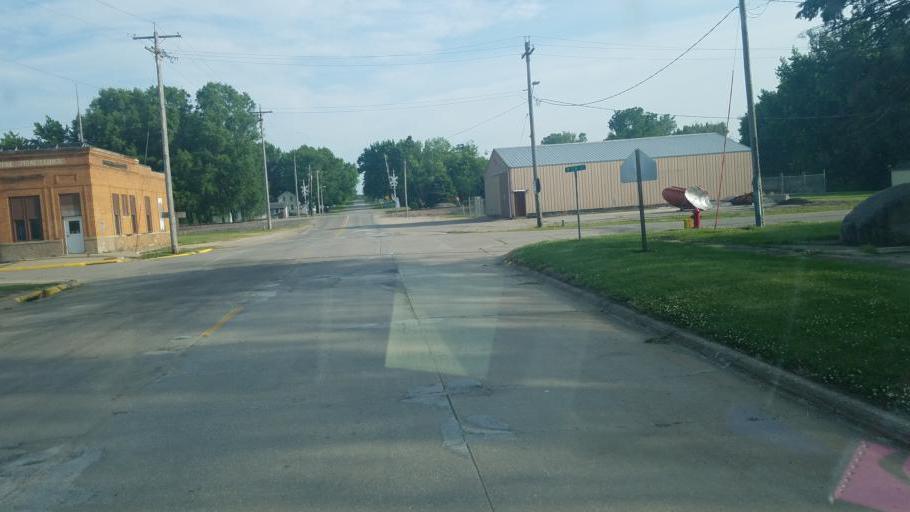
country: US
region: Iowa
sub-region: Tama County
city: Toledo
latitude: 41.9813
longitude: -92.7148
